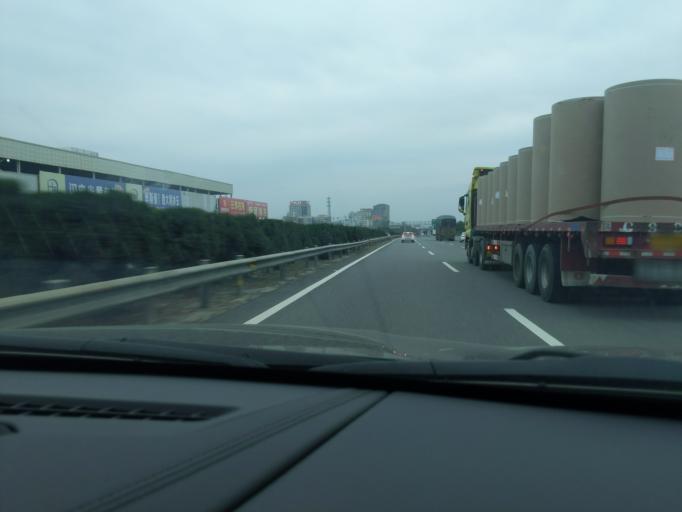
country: CN
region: Fujian
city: Anhai
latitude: 24.7219
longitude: 118.4055
